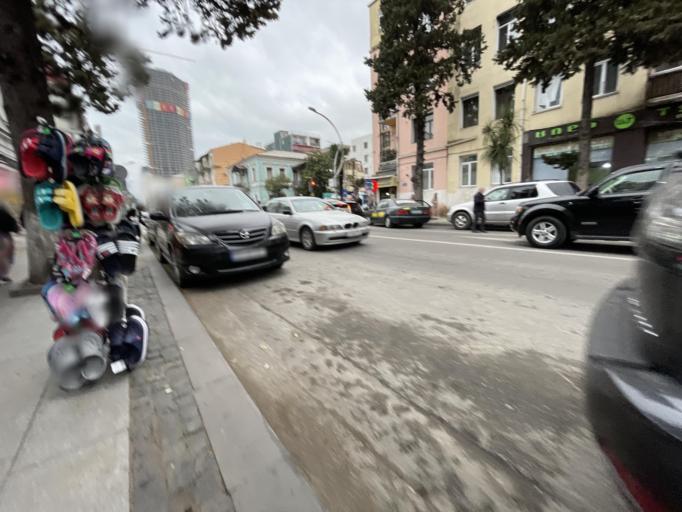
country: GE
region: Ajaria
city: Batumi
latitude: 41.6466
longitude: 41.6307
